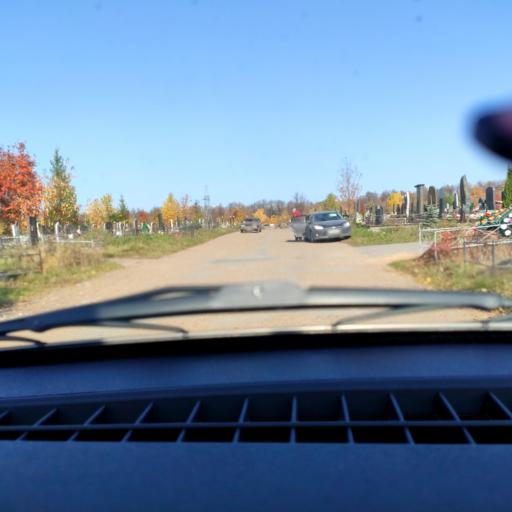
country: RU
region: Bashkortostan
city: Mikhaylovka
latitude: 54.8158
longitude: 55.8665
